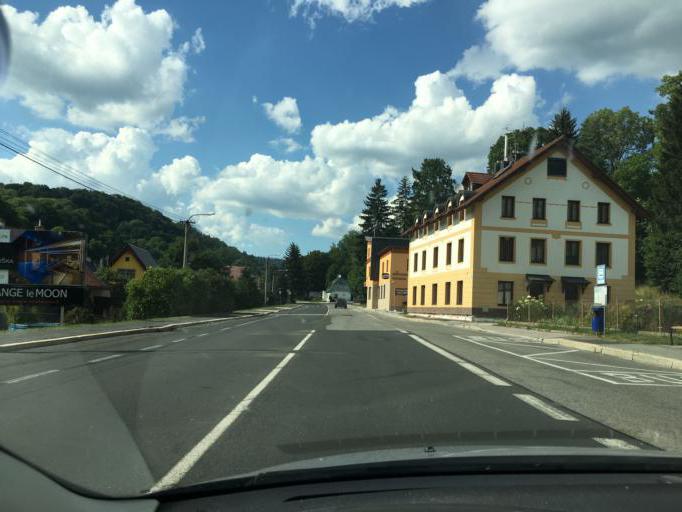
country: CZ
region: Kralovehradecky
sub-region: Okres Trutnov
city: Vrchlabi
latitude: 50.6457
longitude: 15.6079
